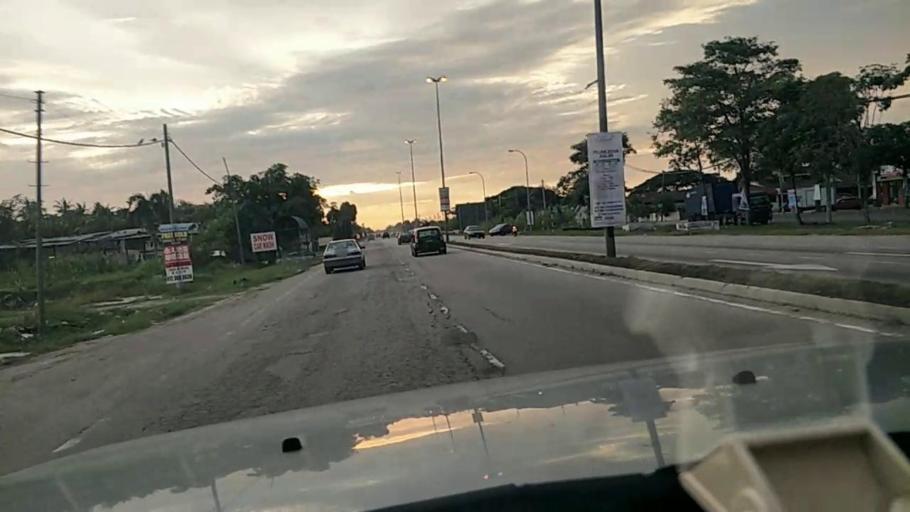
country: MY
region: Perak
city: Kampong Dungun
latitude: 3.1397
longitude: 101.3673
